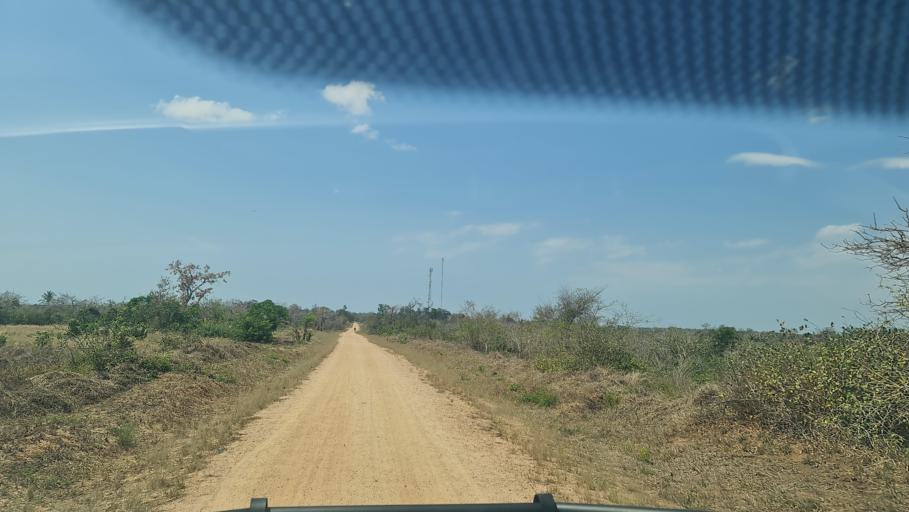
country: MZ
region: Nampula
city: Ilha de Mocambique
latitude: -15.1912
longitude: 40.5216
